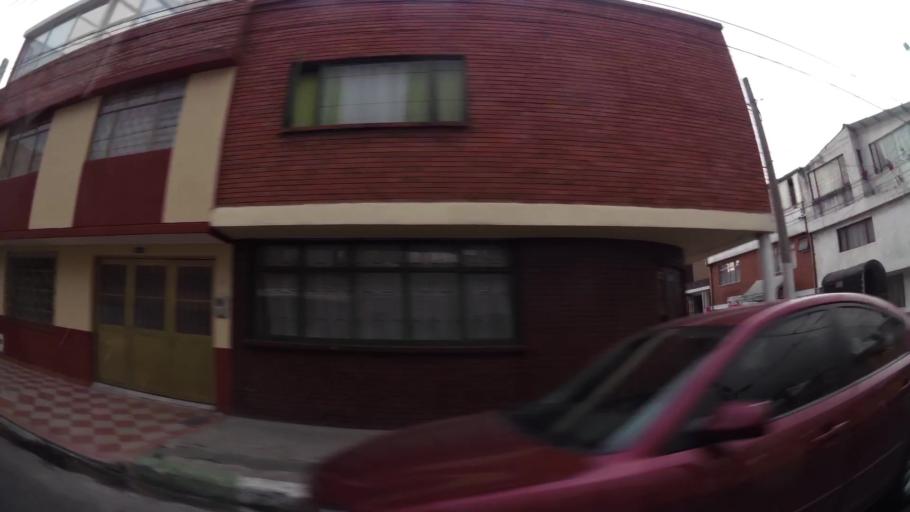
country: CO
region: Bogota D.C.
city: Barrio San Luis
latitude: 4.7216
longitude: -74.0708
